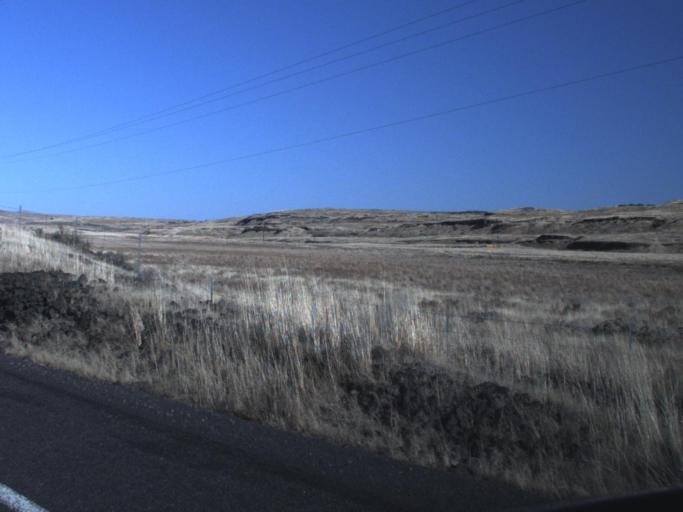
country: US
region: Washington
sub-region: Adams County
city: Ritzville
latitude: 46.7283
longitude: -118.3592
